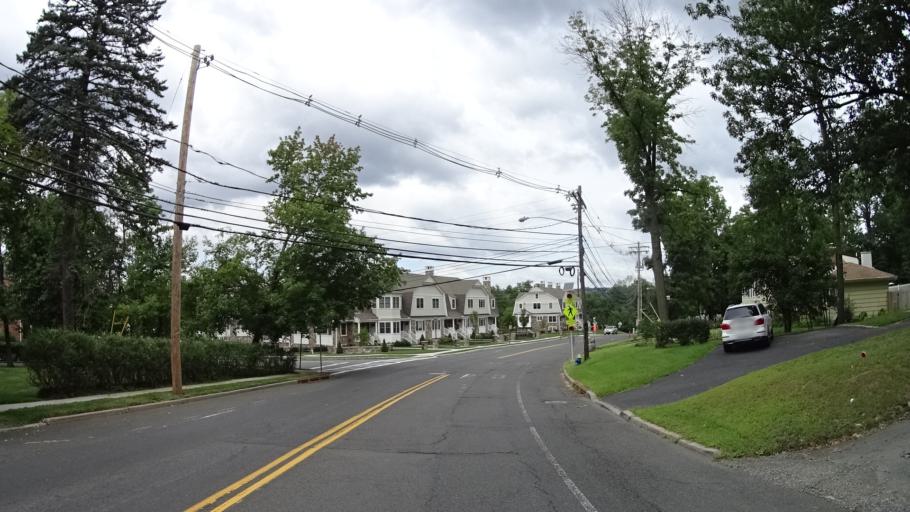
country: US
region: New Jersey
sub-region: Union County
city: New Providence
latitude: 40.6943
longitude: -74.4009
